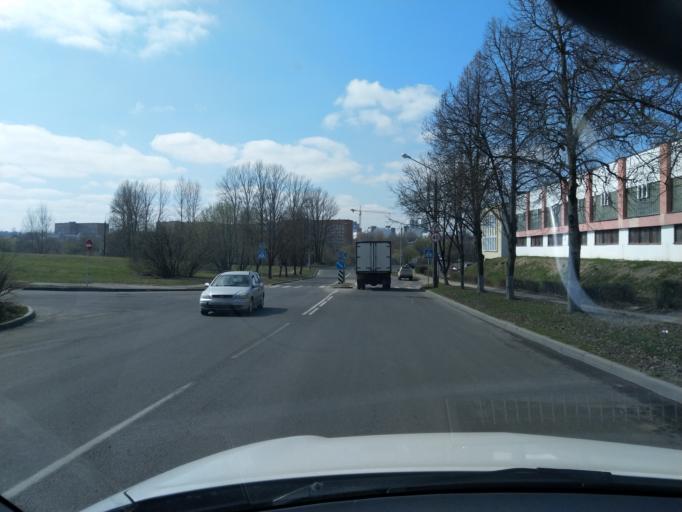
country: BY
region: Minsk
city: Syenitsa
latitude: 53.8645
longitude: 27.5036
